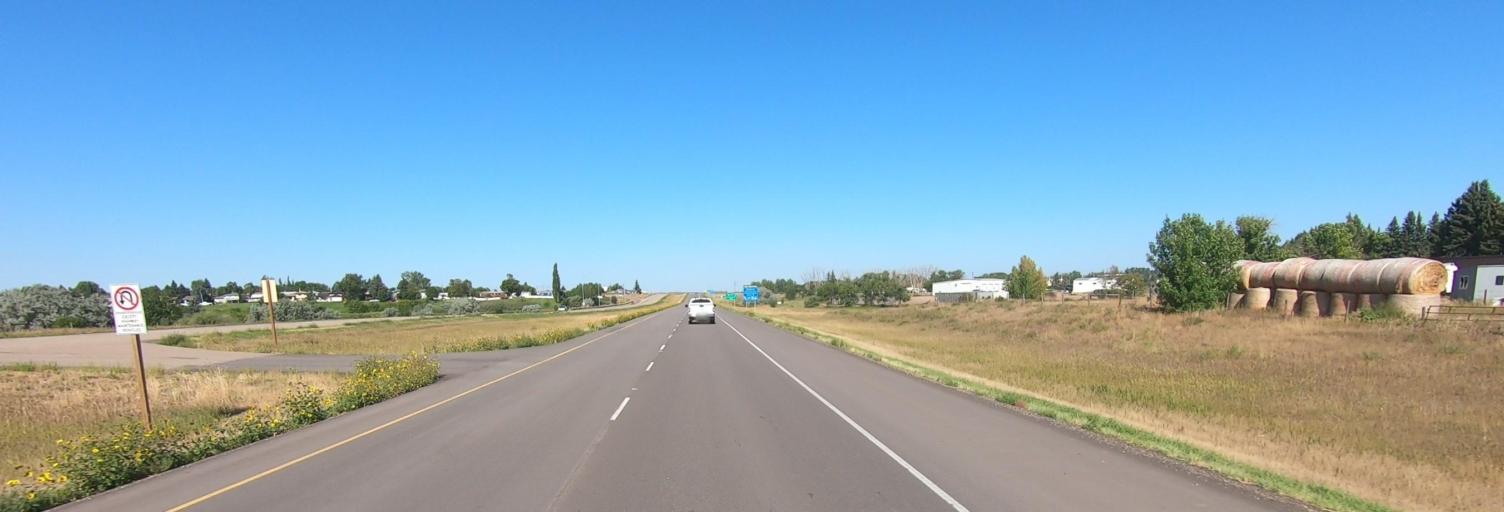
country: CA
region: Alberta
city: Brooks
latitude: 50.5829
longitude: -111.8821
